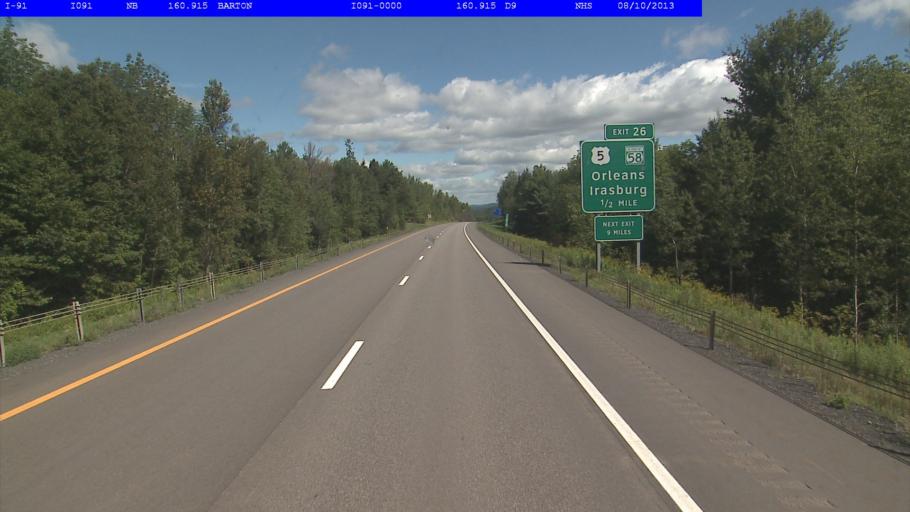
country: US
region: Vermont
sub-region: Orleans County
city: Newport
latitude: 44.7995
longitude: -72.2149
